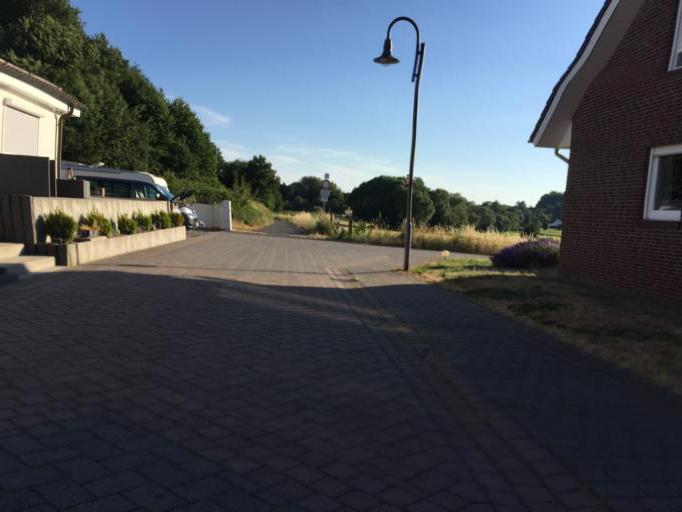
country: DE
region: Rheinland-Pfalz
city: Berod bei Wallmerod
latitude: 50.4799
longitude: 7.9325
